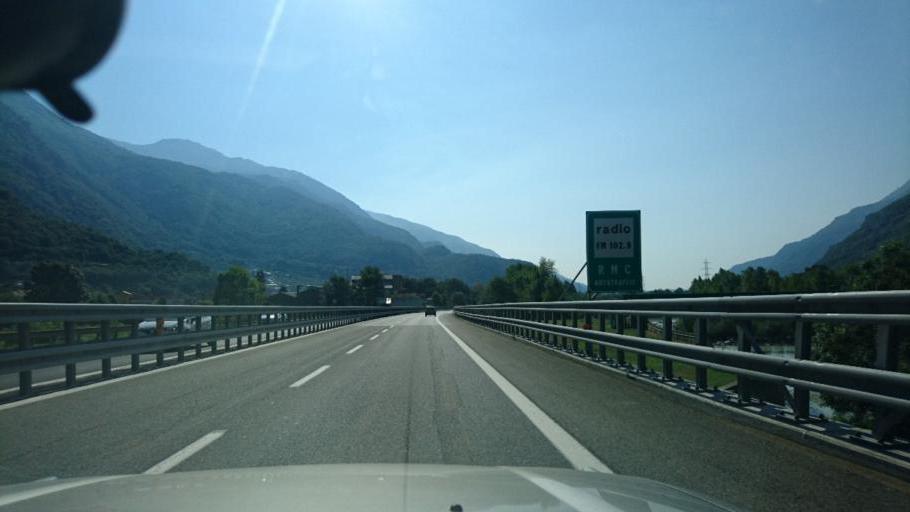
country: IT
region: Aosta Valley
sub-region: Valle d'Aosta
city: Pont-Saint-Martin
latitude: 45.5894
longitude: 7.7940
